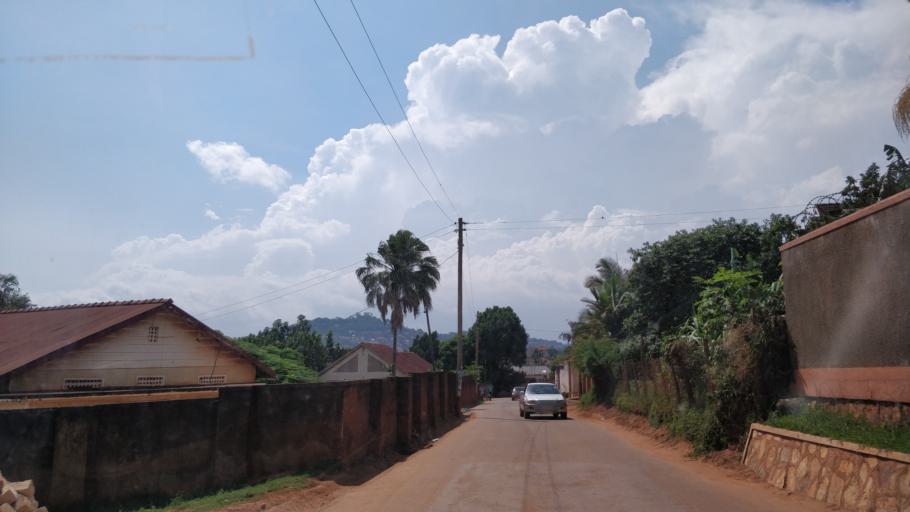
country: UG
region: Central Region
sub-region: Kampala District
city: Kampala
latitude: 0.2837
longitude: 32.6152
